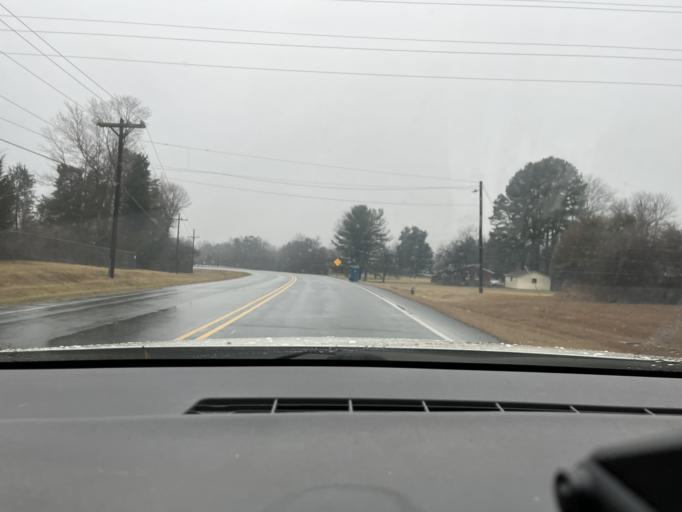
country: US
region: North Carolina
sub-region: Guilford County
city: Pleasant Garden
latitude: 36.0108
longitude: -79.7571
